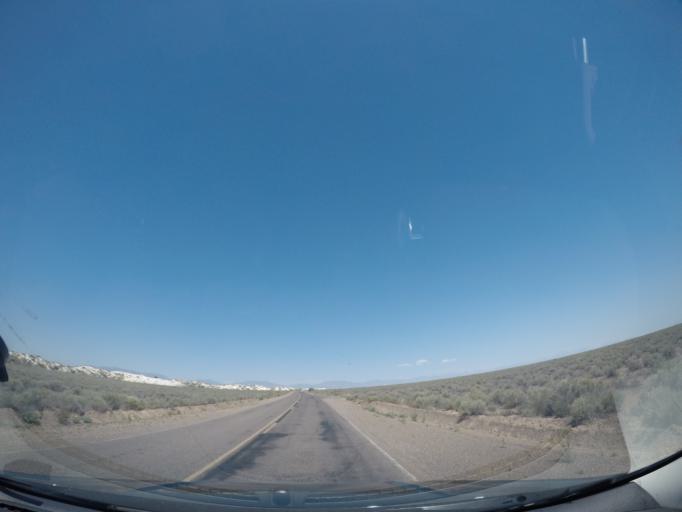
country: US
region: New Mexico
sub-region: Otero County
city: Holloman Air Force Base
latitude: 32.7873
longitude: -106.1855
